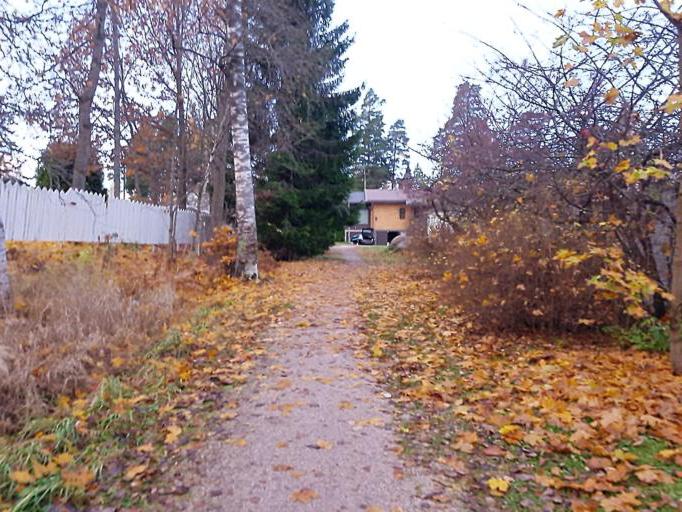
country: FI
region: Uusimaa
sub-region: Helsinki
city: Teekkarikylae
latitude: 60.2555
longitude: 24.8890
